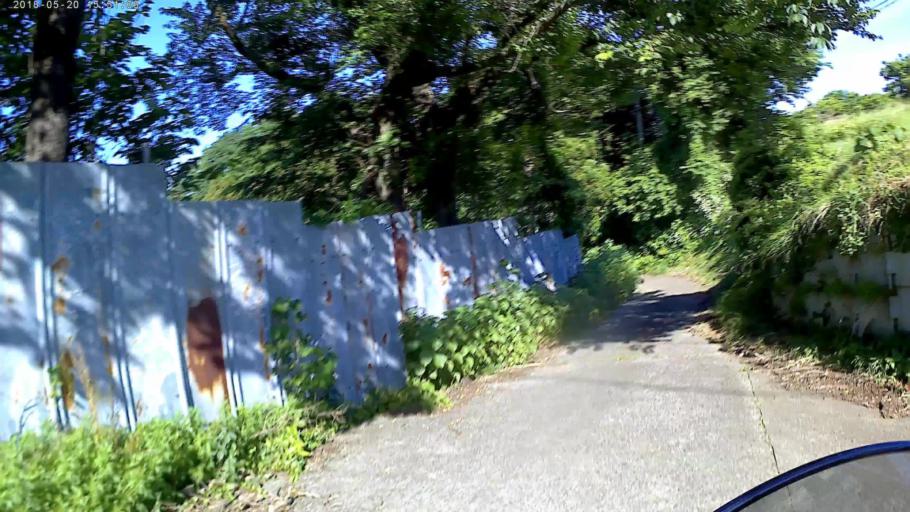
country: JP
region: Kanagawa
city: Hadano
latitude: 35.3248
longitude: 139.1994
